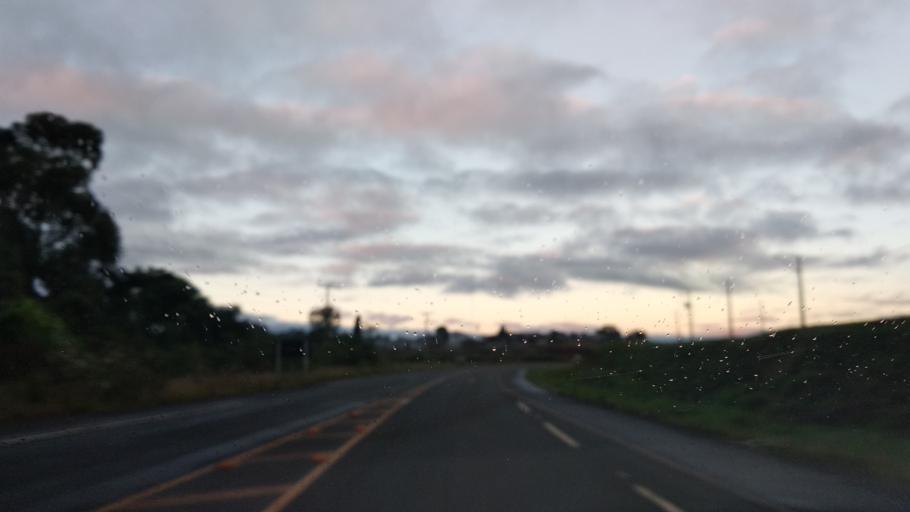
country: BR
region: Santa Catarina
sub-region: Campos Novos
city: Campos Novos
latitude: -27.3748
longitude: -51.2037
